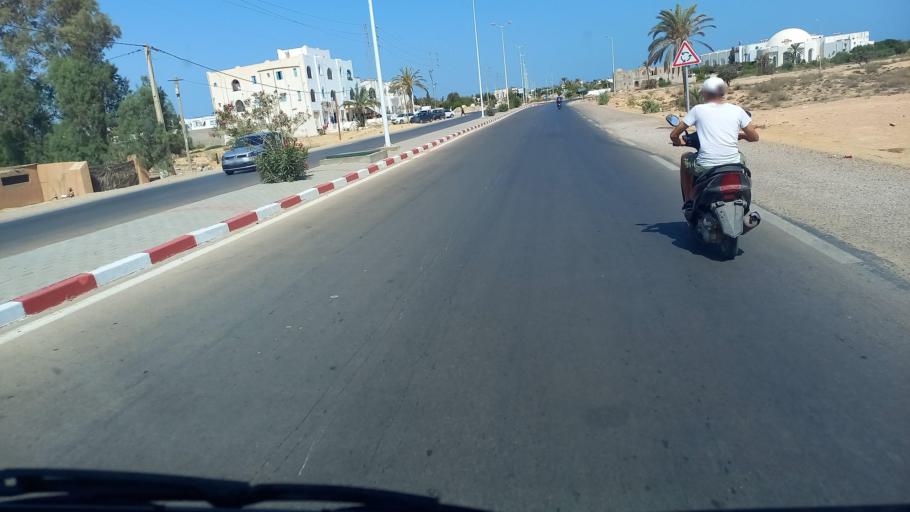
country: TN
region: Madanin
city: Midoun
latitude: 33.8552
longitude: 10.9784
